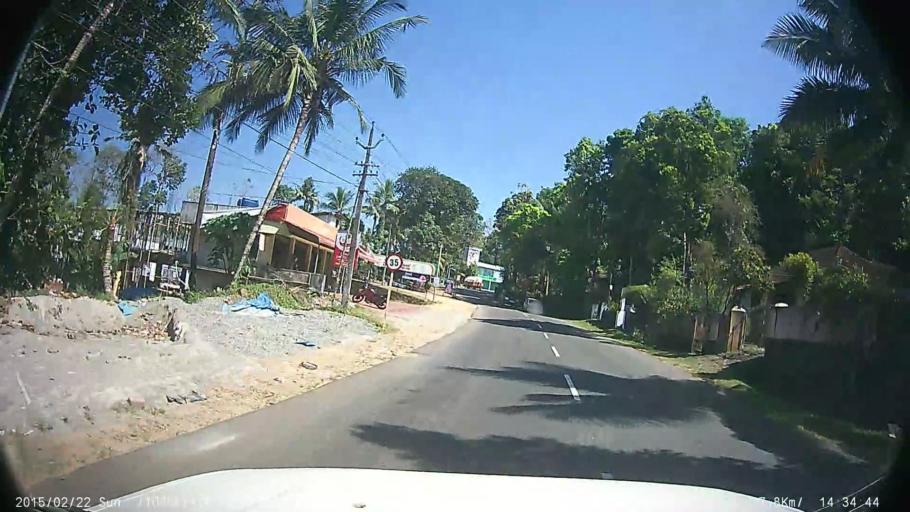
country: IN
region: Kerala
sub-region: Kottayam
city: Erattupetta
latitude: 9.5617
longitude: 76.7776
